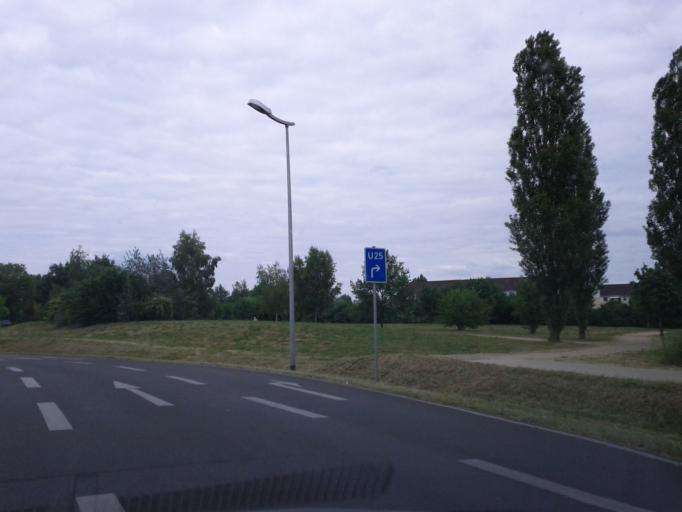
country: DE
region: Berlin
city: Hellersdorf
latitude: 52.5414
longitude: 13.6393
